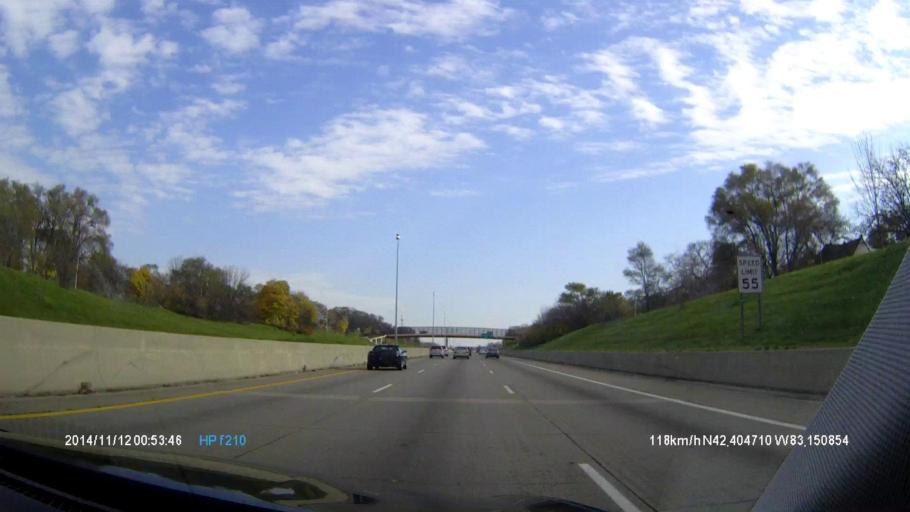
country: US
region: Michigan
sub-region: Wayne County
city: Highland Park
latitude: 42.4047
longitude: -83.1506
